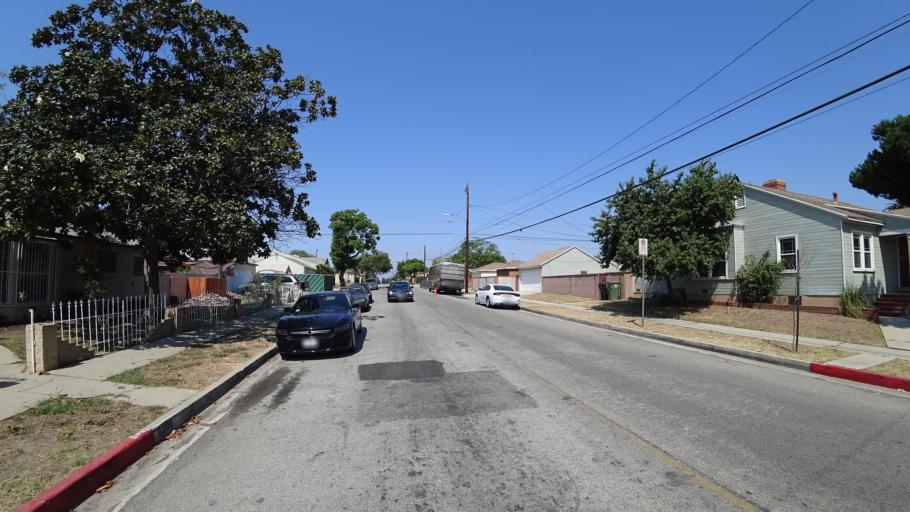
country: US
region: California
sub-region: Los Angeles County
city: Westmont
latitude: 33.9491
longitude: -118.3179
